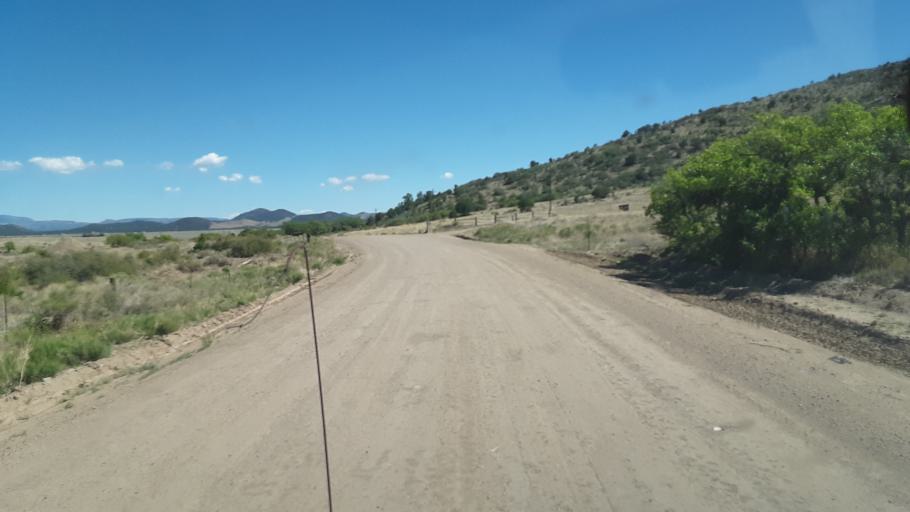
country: US
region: Colorado
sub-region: Custer County
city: Westcliffe
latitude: 38.2413
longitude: -105.5012
